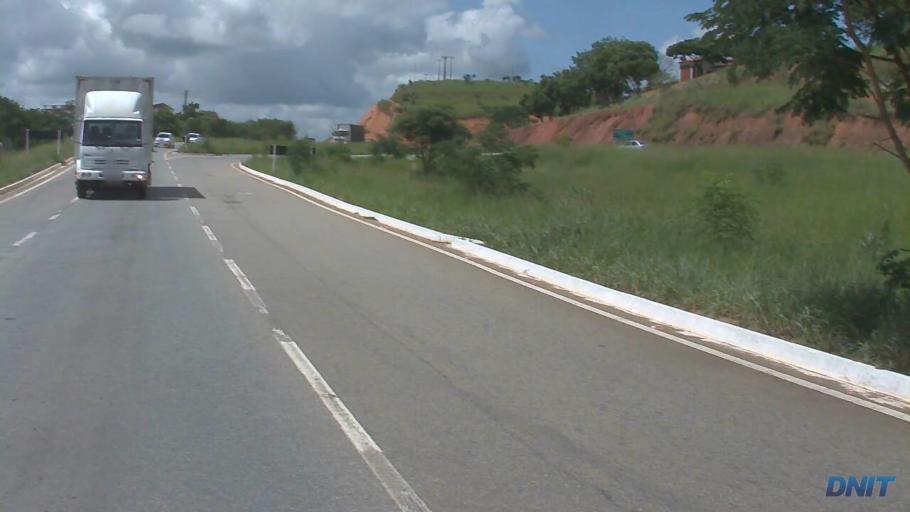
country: BR
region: Minas Gerais
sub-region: Governador Valadares
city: Governador Valadares
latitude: -18.9110
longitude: -42.0076
